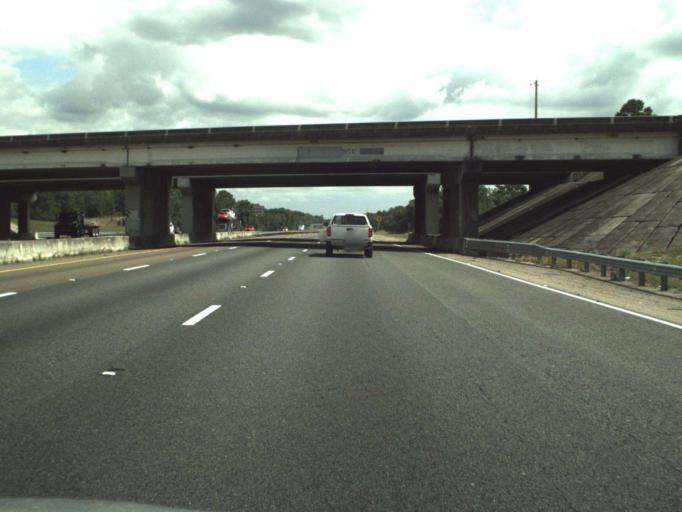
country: US
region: Florida
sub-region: Volusia County
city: Lake Helen
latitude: 28.9545
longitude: -81.2578
